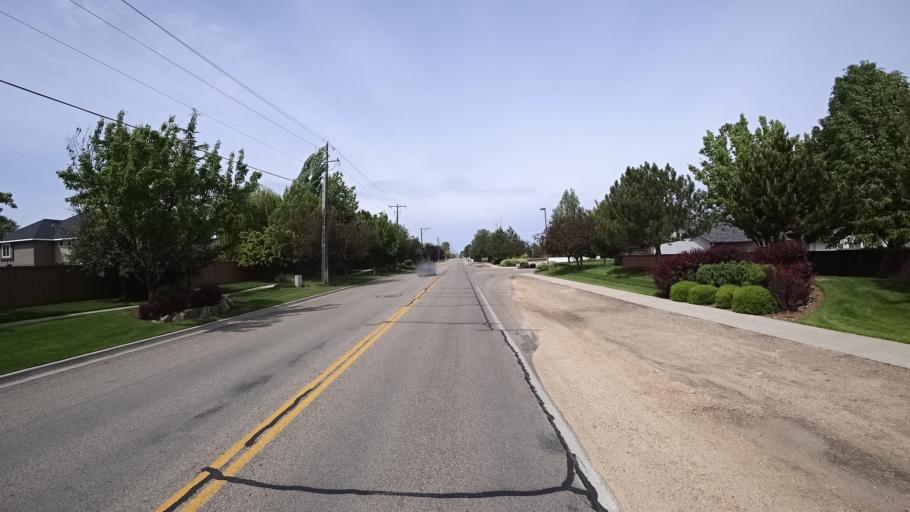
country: US
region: Idaho
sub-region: Ada County
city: Meridian
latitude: 43.5611
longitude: -116.3279
